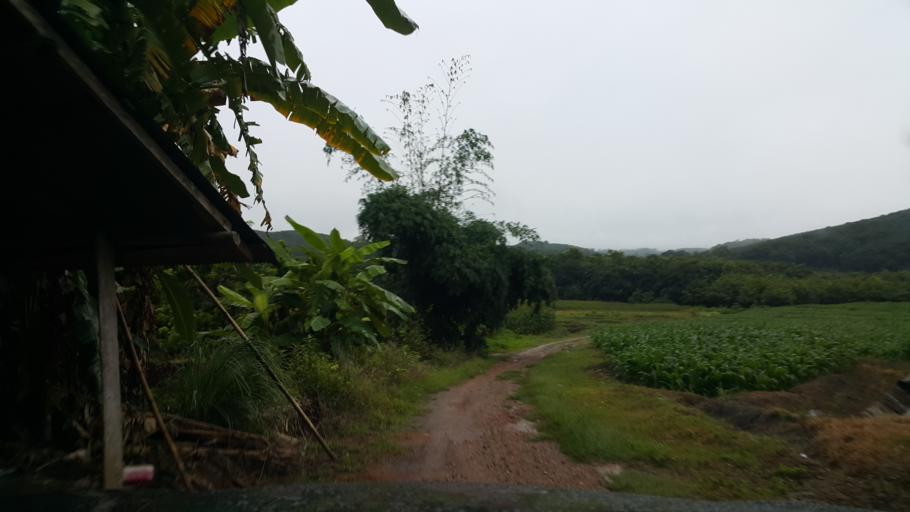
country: TH
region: Phayao
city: Phu Sang
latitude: 19.6242
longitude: 100.4114
